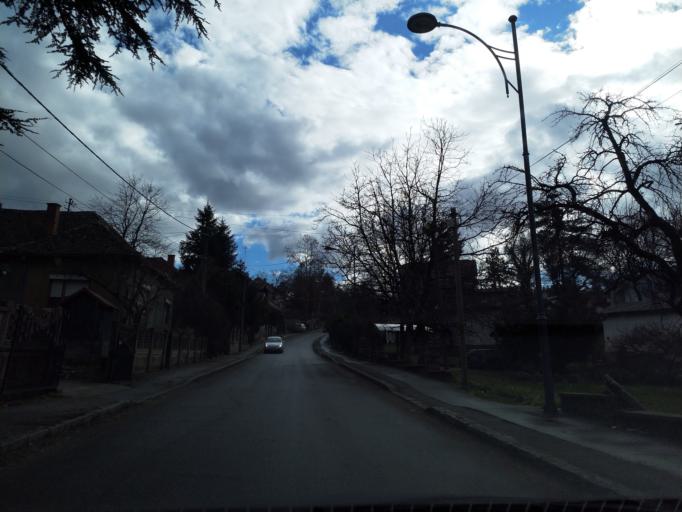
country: RS
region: Central Serbia
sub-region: Belgrade
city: Grocka
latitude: 44.6694
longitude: 20.7185
